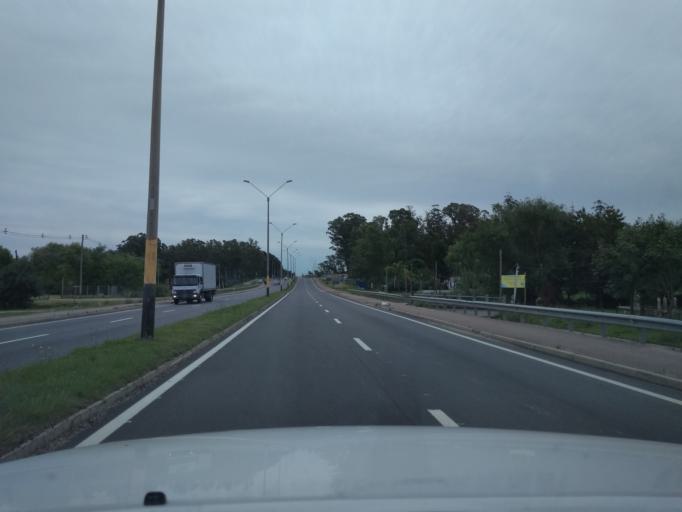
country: UY
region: Canelones
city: Colonia Nicolich
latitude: -34.8101
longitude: -56.0415
